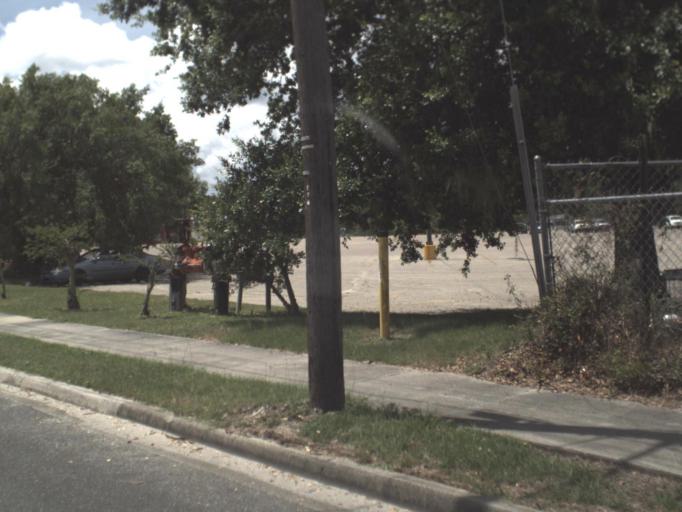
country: US
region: Florida
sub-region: Taylor County
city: Perry
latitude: 30.1008
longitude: -83.5859
